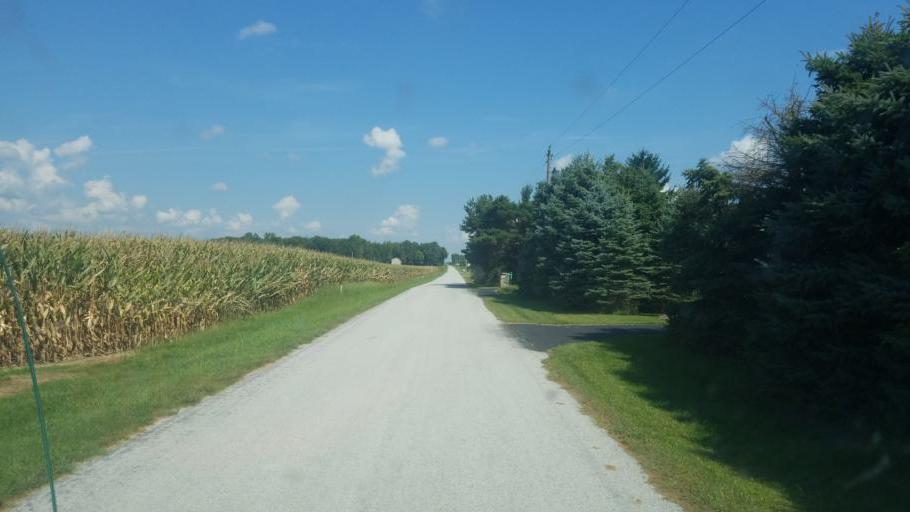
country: US
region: Ohio
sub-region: Hardin County
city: Kenton
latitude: 40.6619
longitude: -83.4957
